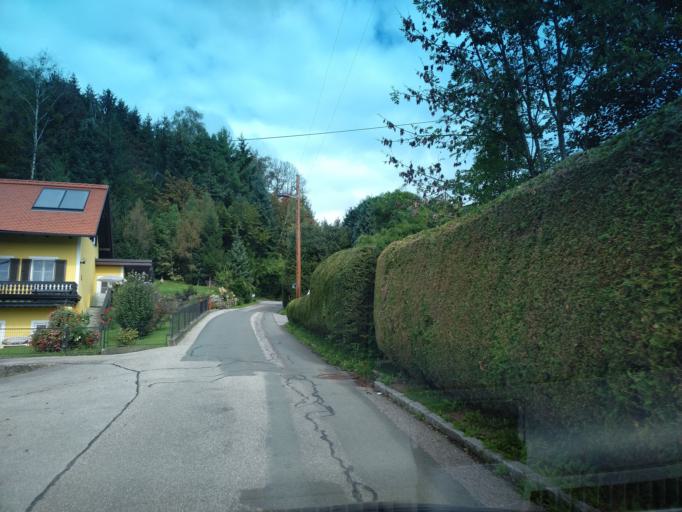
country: AT
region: Styria
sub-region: Politischer Bezirk Deutschlandsberg
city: Deutschlandsberg
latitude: 46.8240
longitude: 15.2141
